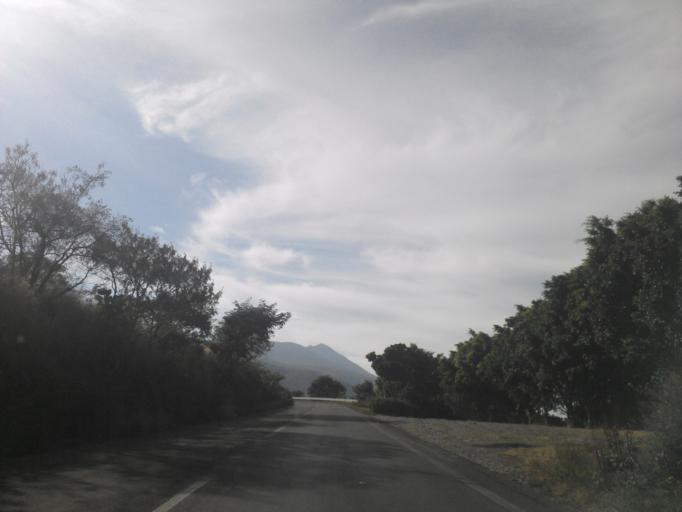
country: MX
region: Jalisco
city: Ixtlahuacan de los Membrillos
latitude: 20.3440
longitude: -103.1850
